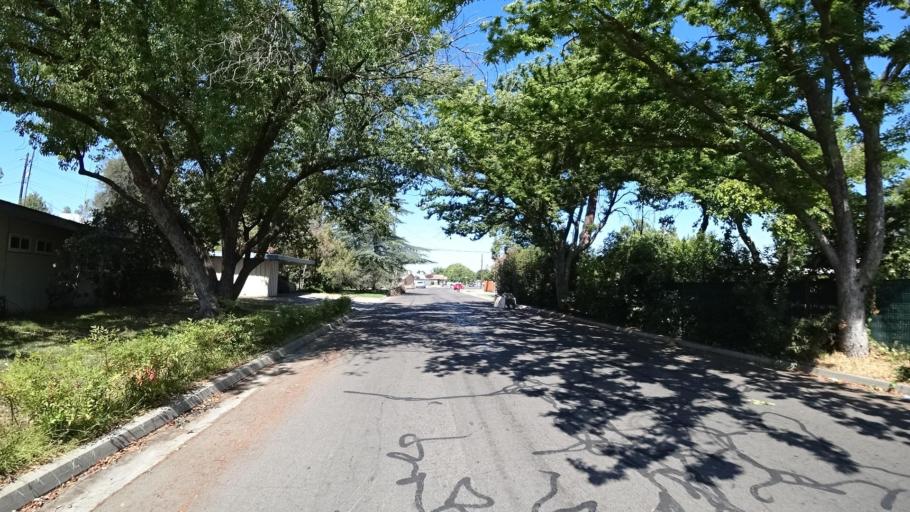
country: US
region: California
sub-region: Fresno County
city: Fresno
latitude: 36.7902
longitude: -119.7763
